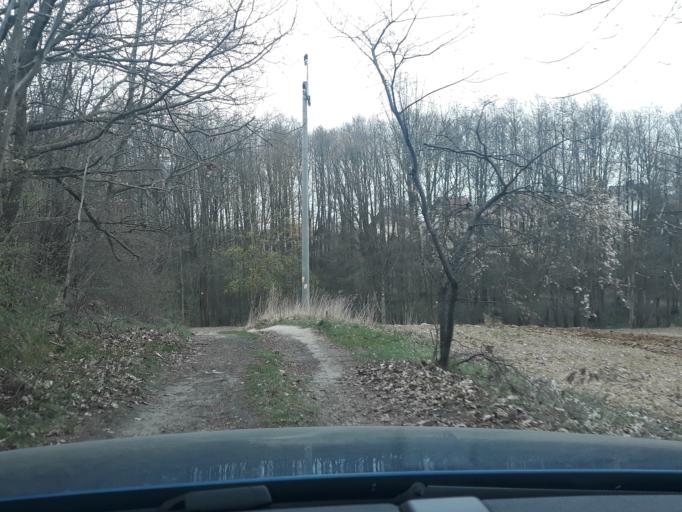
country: PL
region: Pomeranian Voivodeship
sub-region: Powiat chojnicki
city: Chojnice
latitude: 53.7262
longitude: 17.4913
